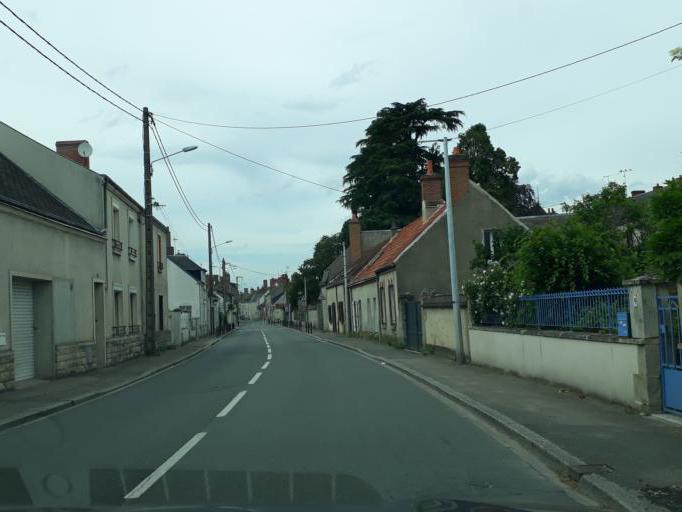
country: FR
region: Centre
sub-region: Departement du Loiret
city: Jargeau
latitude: 47.8620
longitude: 2.1228
